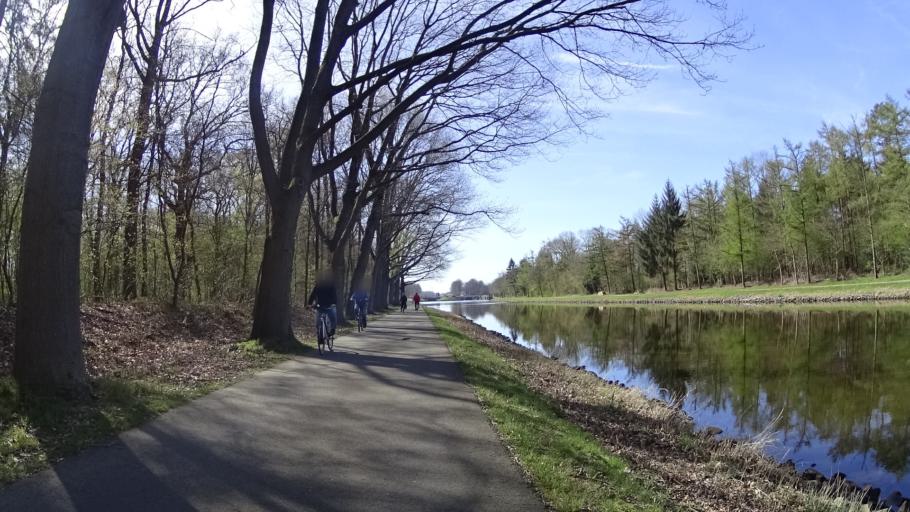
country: DE
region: Lower Saxony
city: Geeste
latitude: 52.6295
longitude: 7.3077
